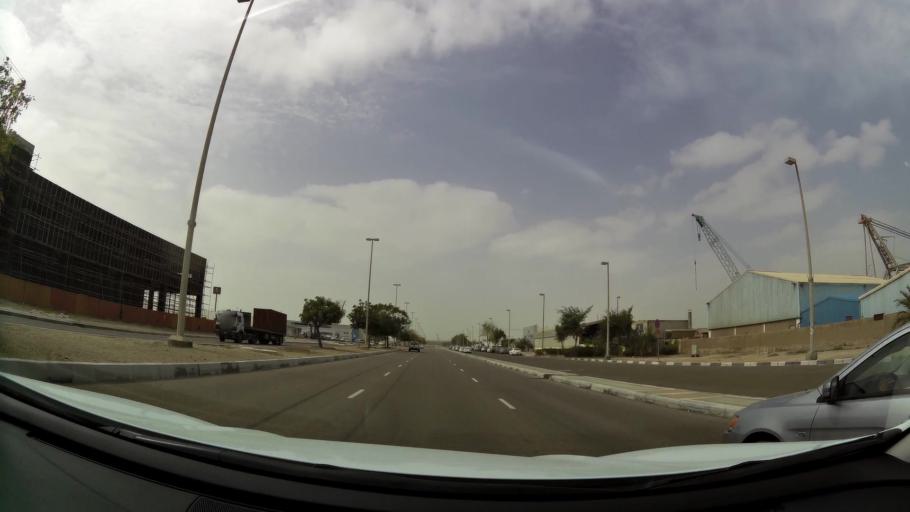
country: AE
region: Abu Dhabi
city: Abu Dhabi
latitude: 24.3811
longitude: 54.4797
